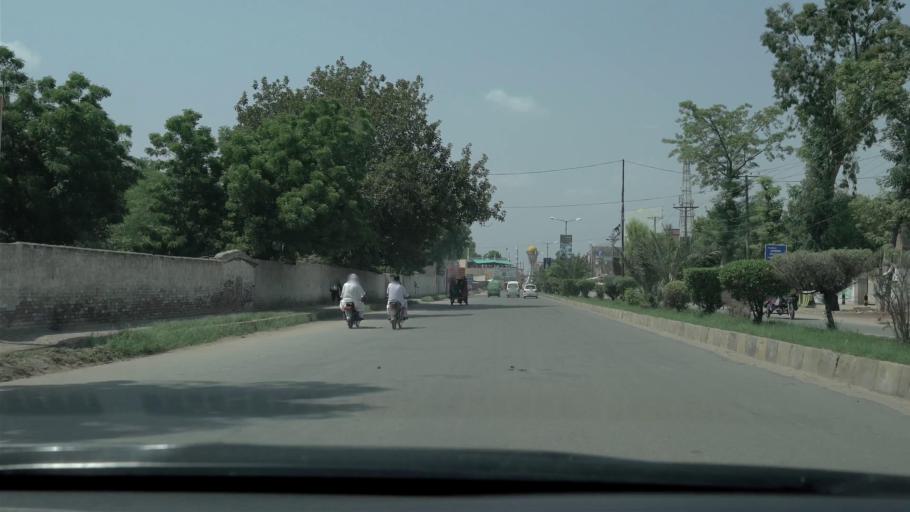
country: PK
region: Punjab
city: Gojra
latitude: 31.1539
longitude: 72.6705
